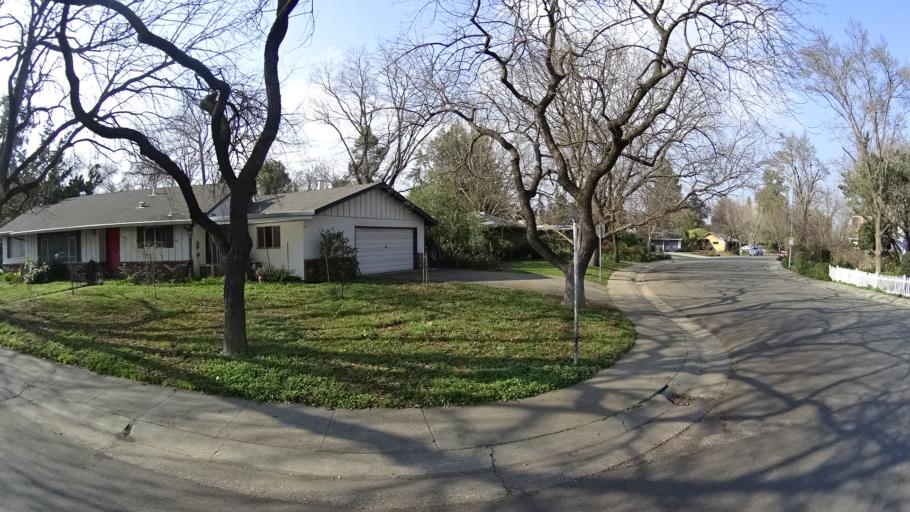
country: US
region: California
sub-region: Yolo County
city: Davis
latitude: 38.5526
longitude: -121.7486
